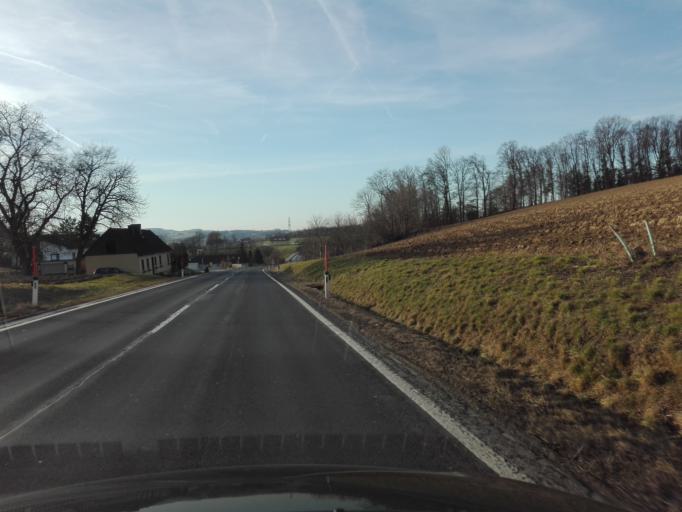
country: AT
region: Lower Austria
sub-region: Politischer Bezirk Amstetten
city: Strengberg
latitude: 48.1475
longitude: 14.6315
